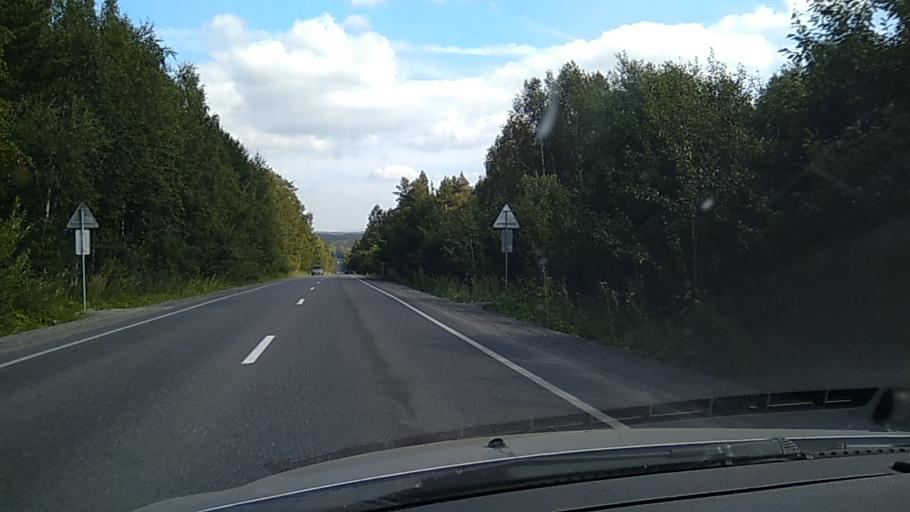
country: RU
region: Chelyabinsk
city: Syrostan
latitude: 55.1203
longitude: 59.8233
